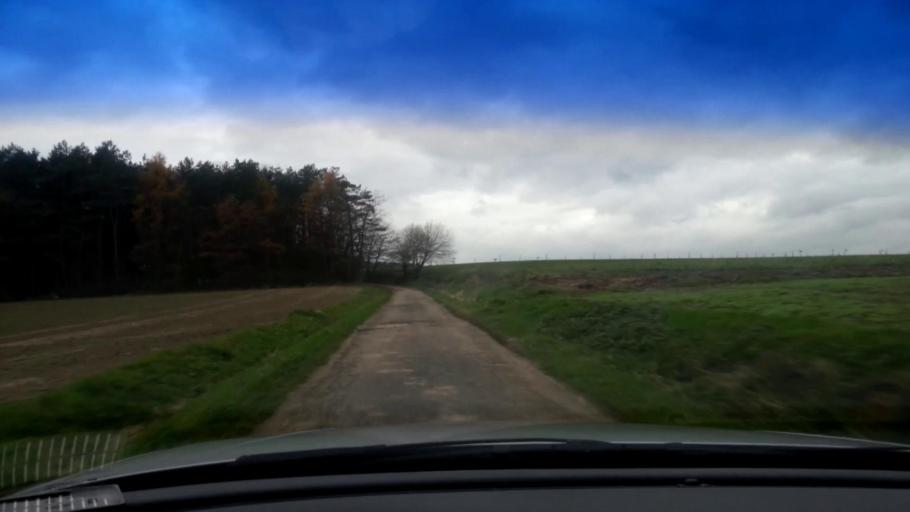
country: DE
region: Bavaria
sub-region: Upper Franconia
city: Stegaurach
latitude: 49.8577
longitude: 10.8135
